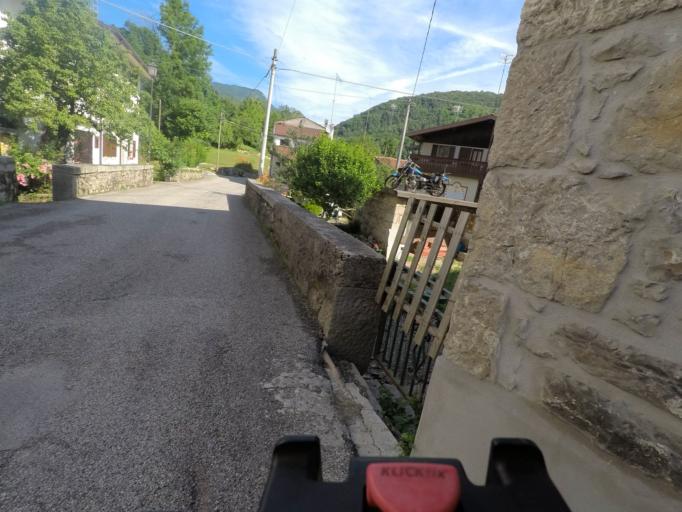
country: IT
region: Friuli Venezia Giulia
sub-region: Provincia di Udine
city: Pulfero
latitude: 46.1699
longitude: 13.4849
